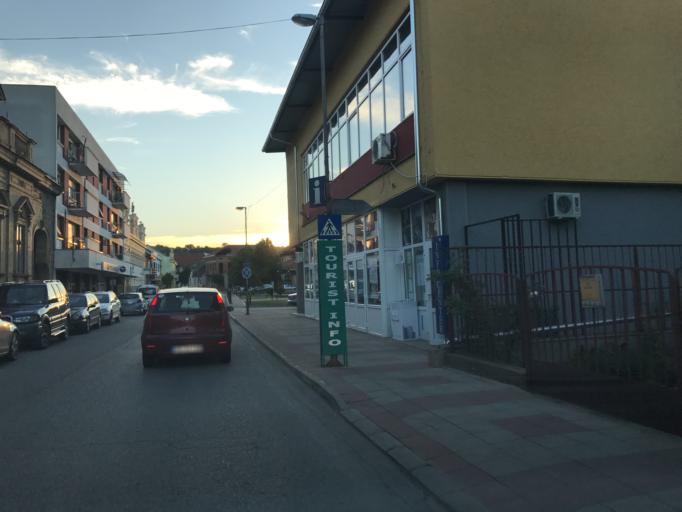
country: RS
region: Central Serbia
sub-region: Branicevski Okrug
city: Golubac
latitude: 44.6533
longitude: 21.6293
